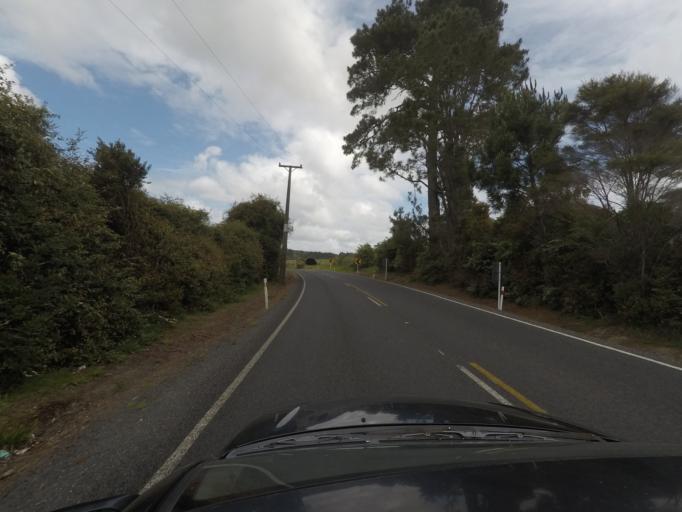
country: NZ
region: Auckland
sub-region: Auckland
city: Parakai
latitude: -36.6538
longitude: 174.5219
